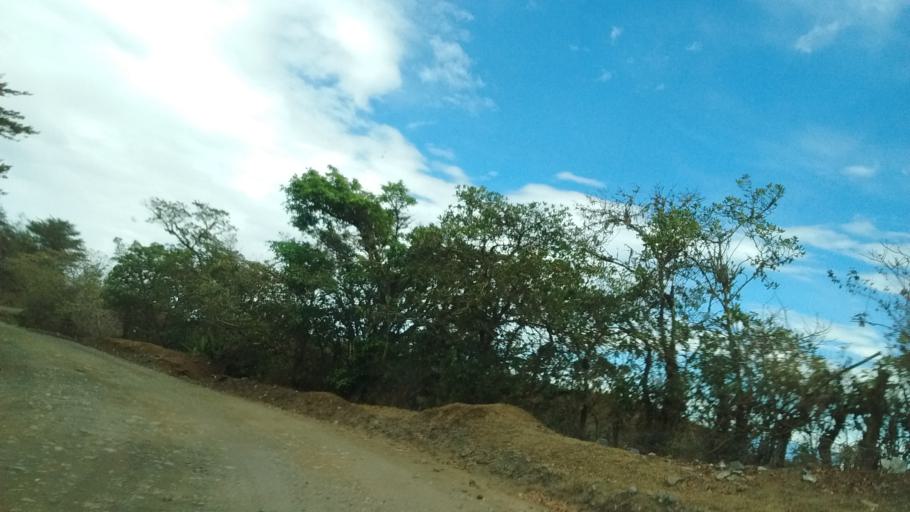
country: CO
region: Cauca
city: Almaguer
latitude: 1.8624
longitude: -76.9305
